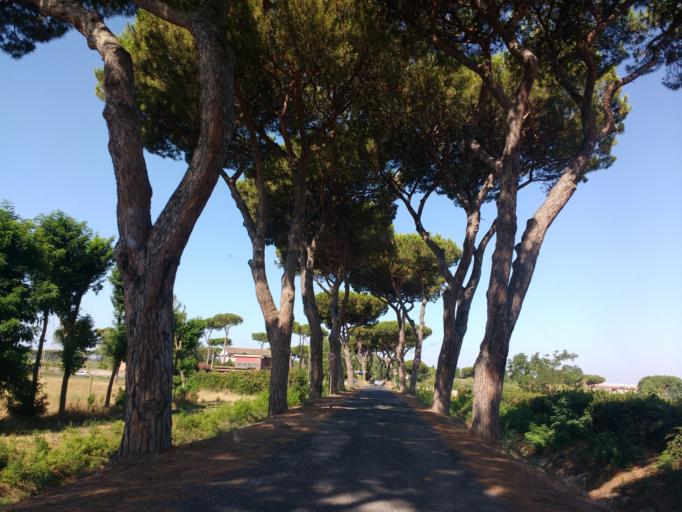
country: IT
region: Latium
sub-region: Citta metropolitana di Roma Capitale
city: Acilia-Castel Fusano-Ostia Antica
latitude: 41.7519
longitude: 12.3315
